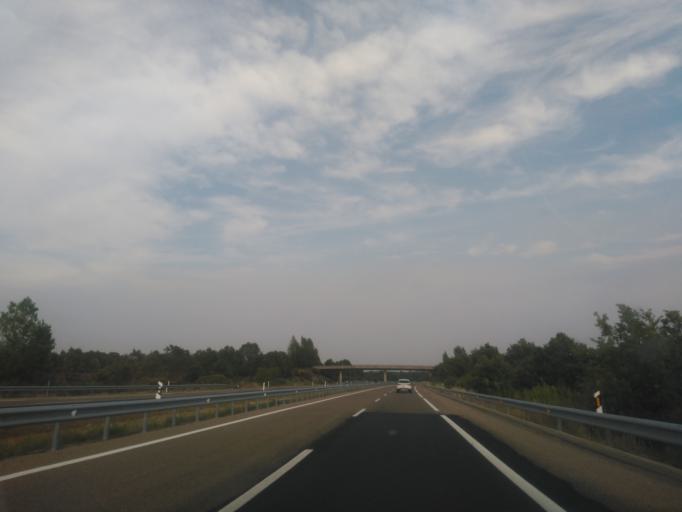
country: ES
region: Castille and Leon
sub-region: Provincia de Zamora
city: Cernadilla
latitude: 42.0384
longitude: -6.4483
